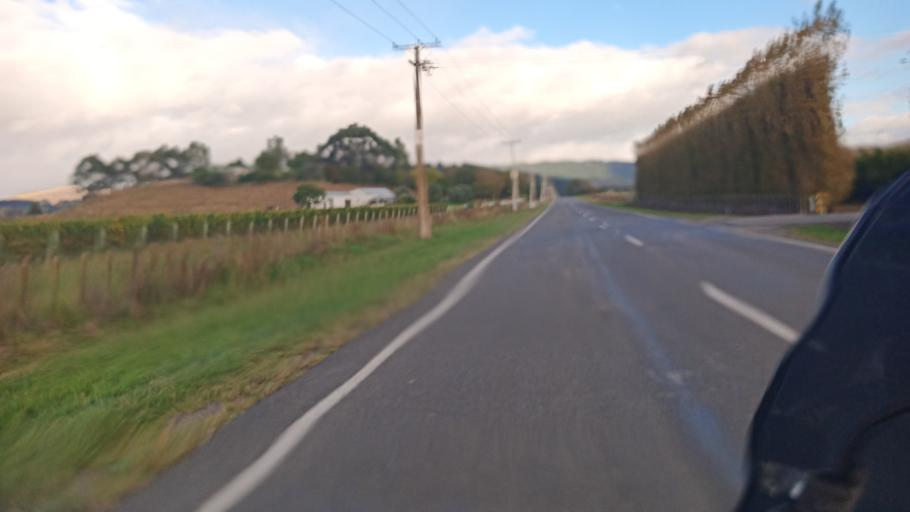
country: NZ
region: Gisborne
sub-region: Gisborne District
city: Gisborne
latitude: -38.6329
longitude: 177.8722
